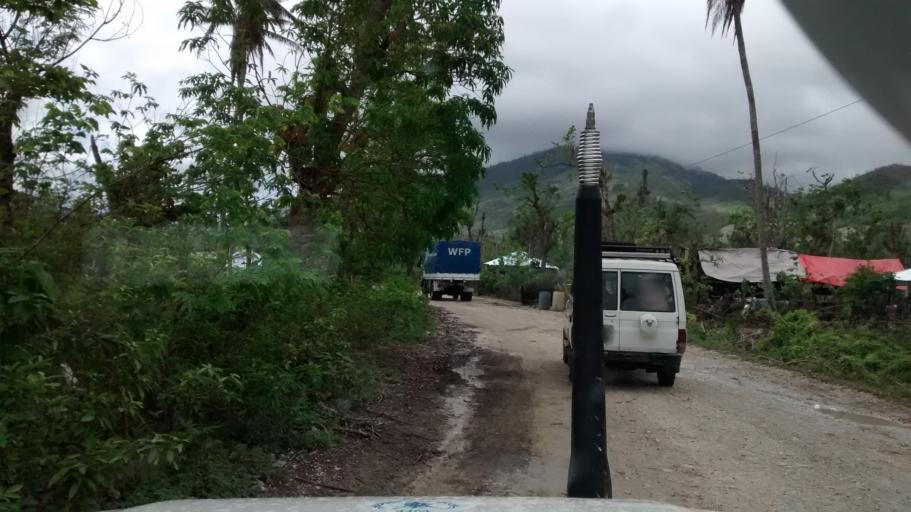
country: HT
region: Grandans
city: Moron
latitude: 18.5984
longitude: -74.1947
